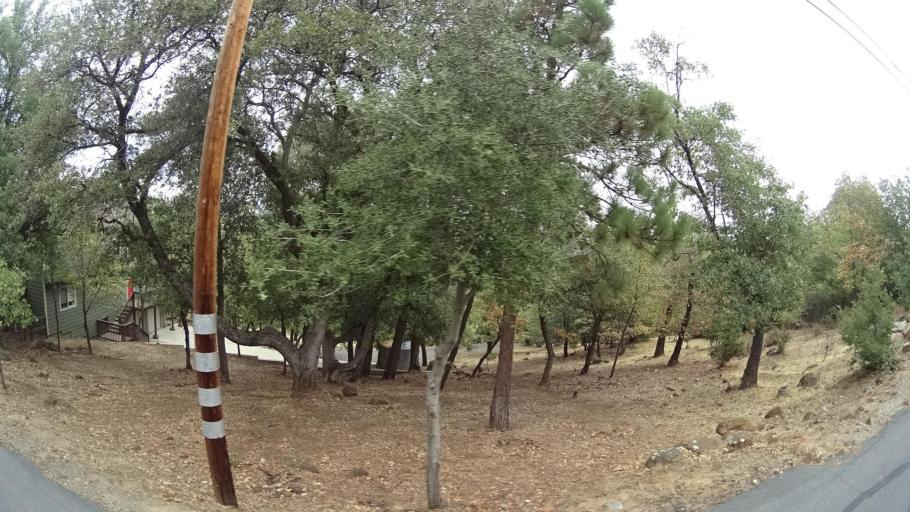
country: US
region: California
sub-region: San Diego County
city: Julian
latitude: 33.0516
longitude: -116.6285
